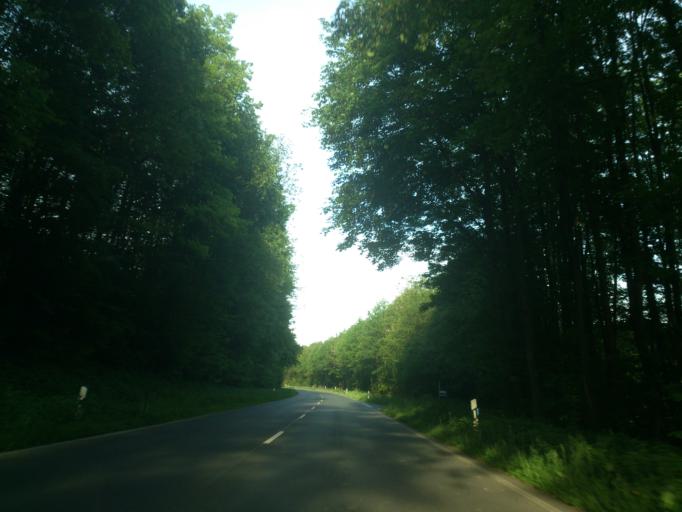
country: DE
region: North Rhine-Westphalia
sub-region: Regierungsbezirk Detmold
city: Altenbeken
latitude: 51.7607
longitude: 8.9170
